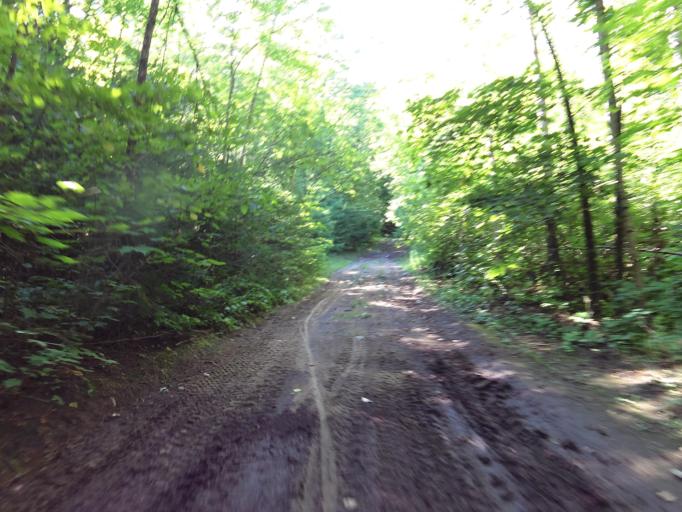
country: CA
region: Ontario
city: Renfrew
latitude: 45.1269
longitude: -76.7403
